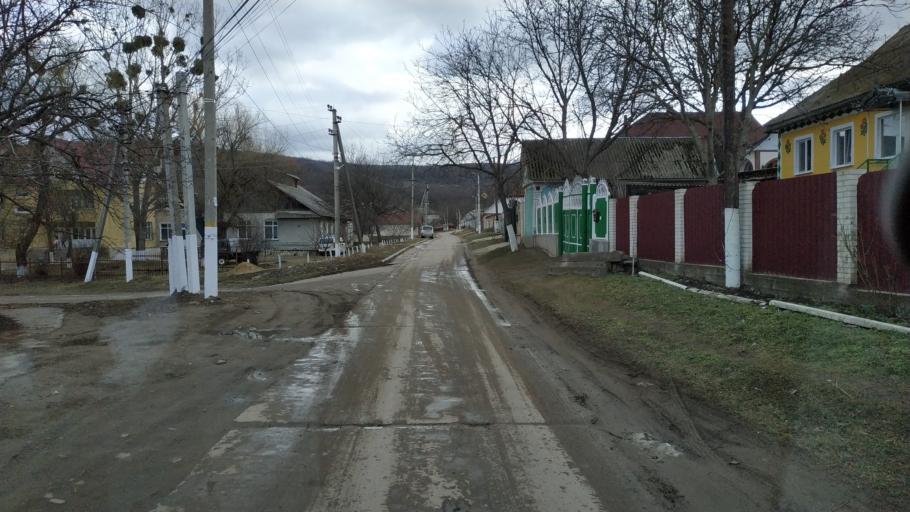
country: MD
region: Stinga Nistrului
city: Bucovat
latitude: 47.1324
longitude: 28.3846
